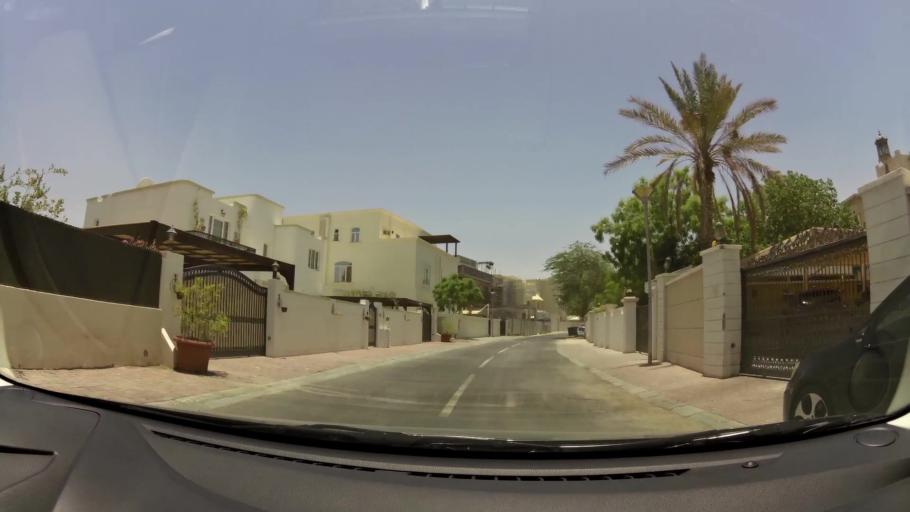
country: OM
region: Muhafazat Masqat
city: Bawshar
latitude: 23.6014
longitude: 58.4572
